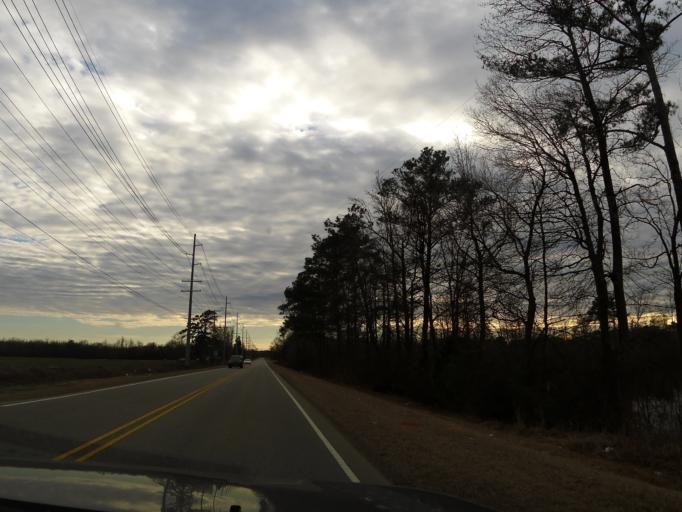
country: US
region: North Carolina
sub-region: Nash County
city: Rocky Mount
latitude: 35.9729
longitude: -77.7790
